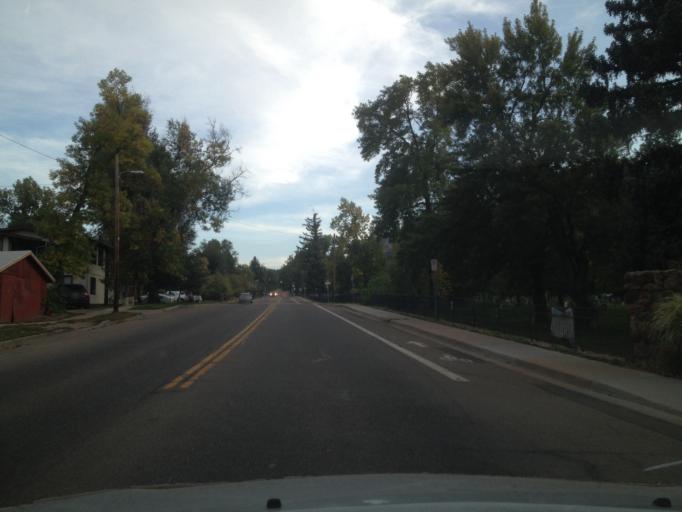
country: US
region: Colorado
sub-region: Boulder County
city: Boulder
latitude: 40.0094
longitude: -105.2820
